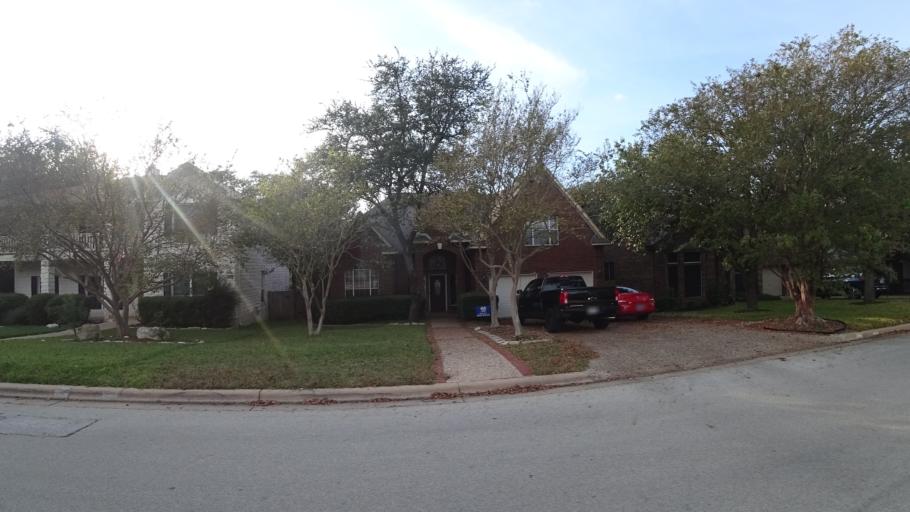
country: US
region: Texas
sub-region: Travis County
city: Hudson Bend
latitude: 30.3782
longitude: -97.8882
